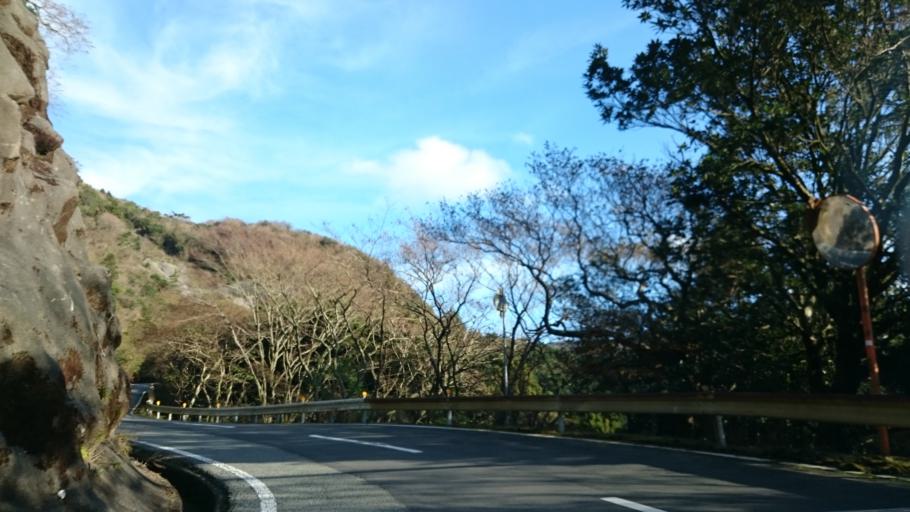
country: JP
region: Shizuoka
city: Heda
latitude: 34.9733
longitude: 138.8301
